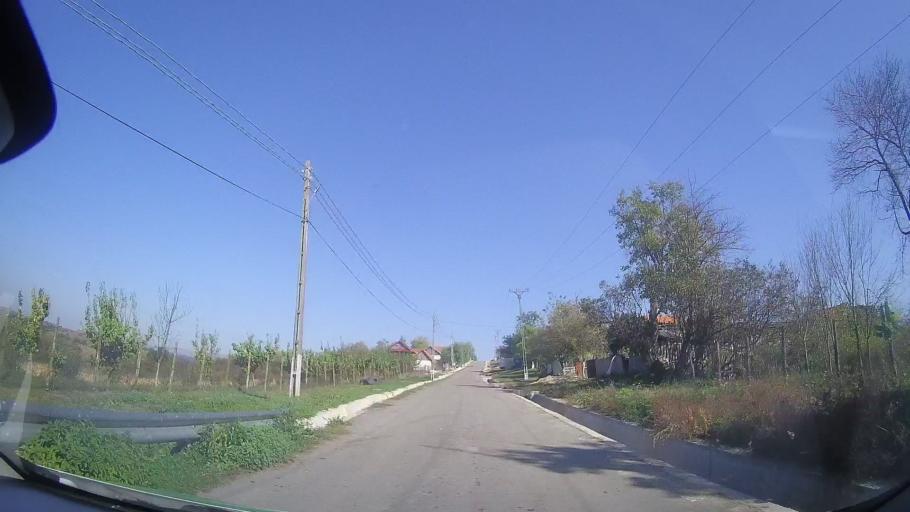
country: RO
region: Timis
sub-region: Comuna Ohaba Lunga
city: Ohaba Lunga
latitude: 45.9074
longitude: 21.9377
